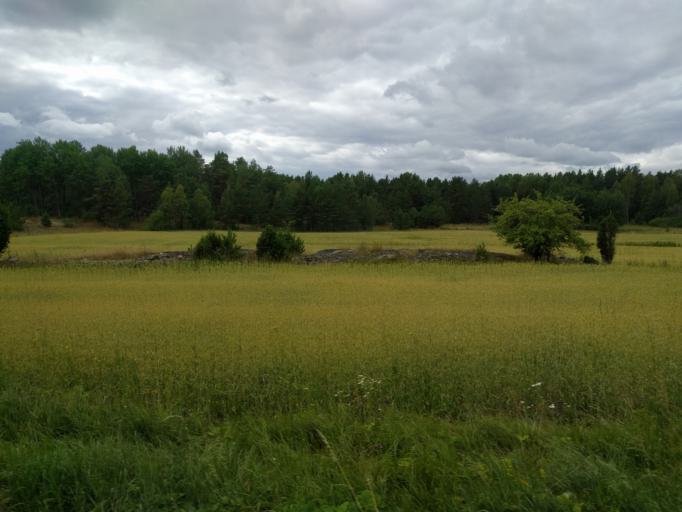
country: SE
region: Soedermanland
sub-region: Nykopings Kommun
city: Svalsta
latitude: 58.4966
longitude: 16.8835
